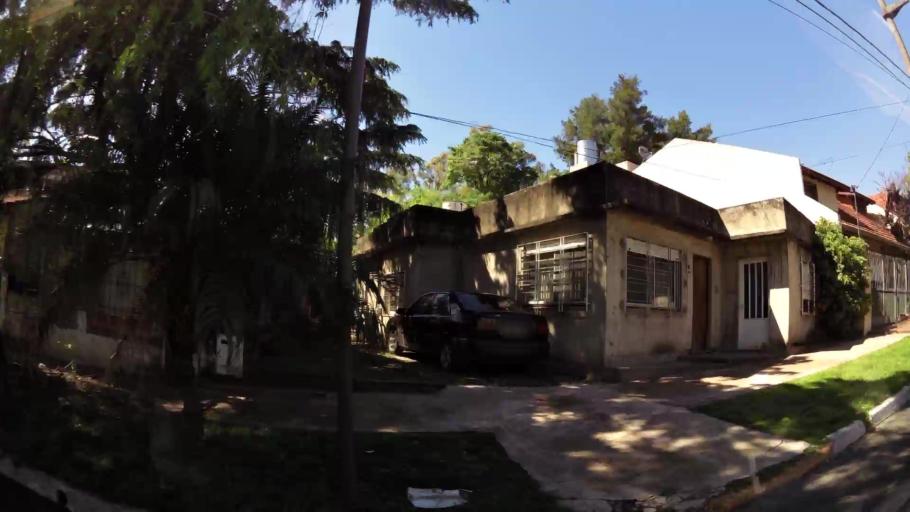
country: AR
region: Buenos Aires
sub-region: Partido de Quilmes
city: Quilmes
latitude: -34.7016
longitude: -58.2875
